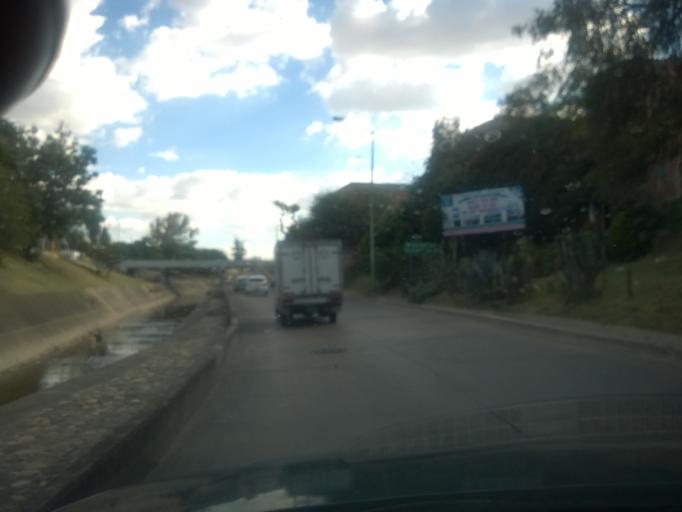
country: MX
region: Guanajuato
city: Leon
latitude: 21.1436
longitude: -101.6803
